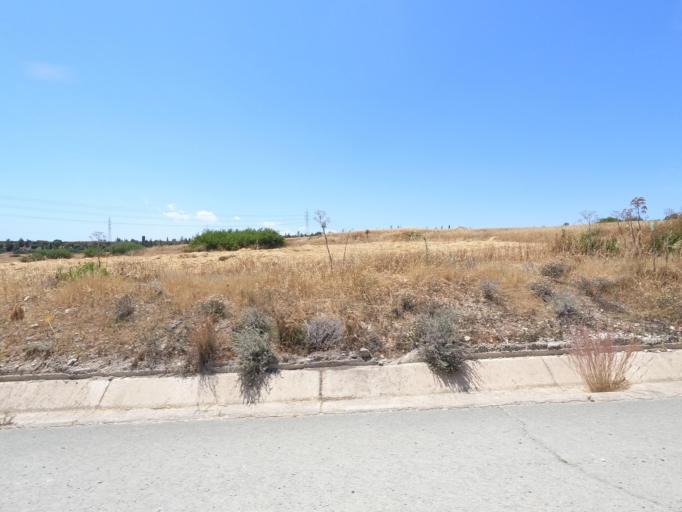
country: CY
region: Larnaka
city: Pyla
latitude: 35.0033
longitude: 33.7035
